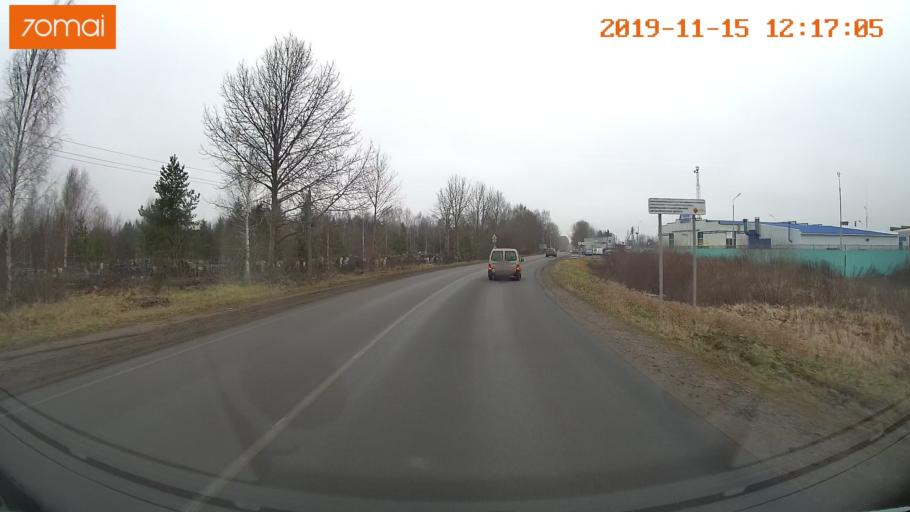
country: RU
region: Vologda
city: Vologda
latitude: 59.1768
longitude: 39.8294
